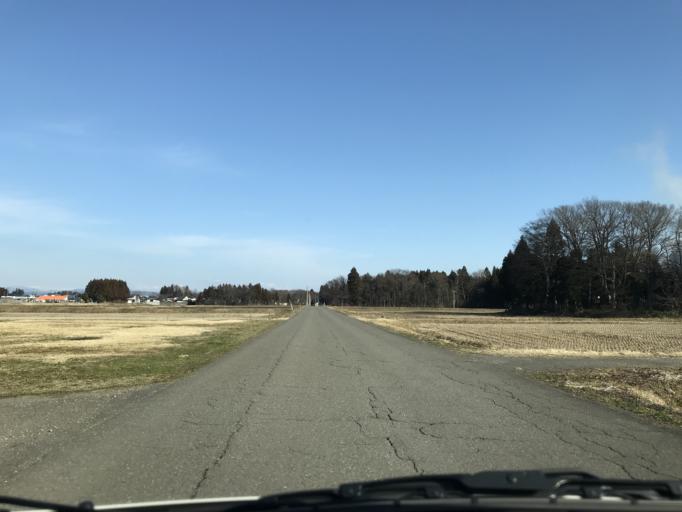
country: JP
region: Iwate
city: Kitakami
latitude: 39.2983
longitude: 141.0185
